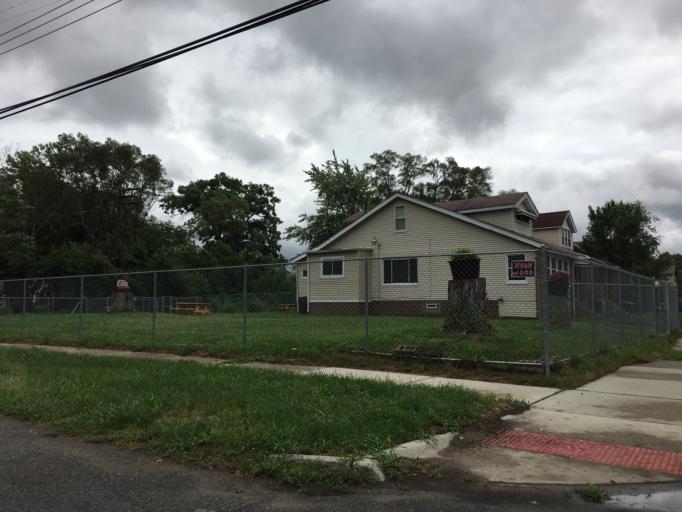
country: US
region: Michigan
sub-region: Wayne County
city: Highland Park
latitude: 42.4062
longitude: -83.1461
